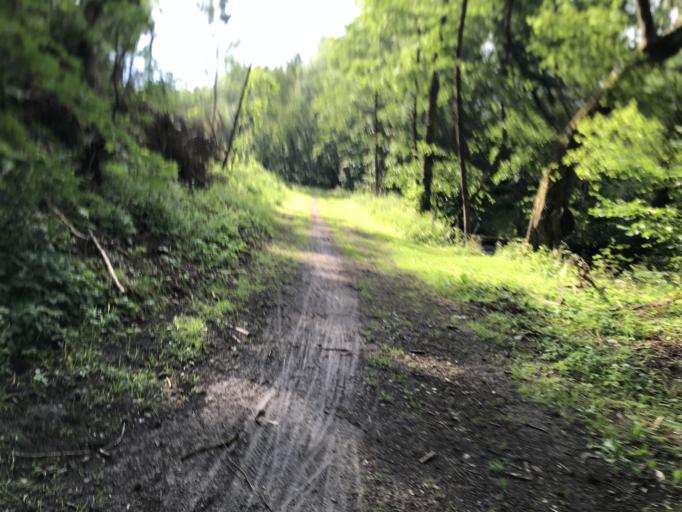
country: DE
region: Hesse
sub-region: Regierungsbezirk Giessen
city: Grunberg
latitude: 50.5461
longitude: 8.9160
